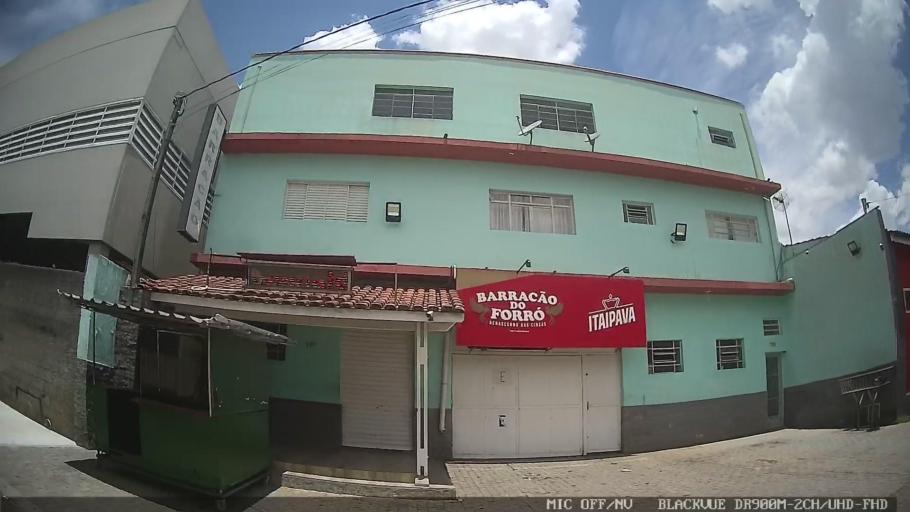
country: BR
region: Sao Paulo
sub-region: Atibaia
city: Atibaia
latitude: -23.1136
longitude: -46.5662
